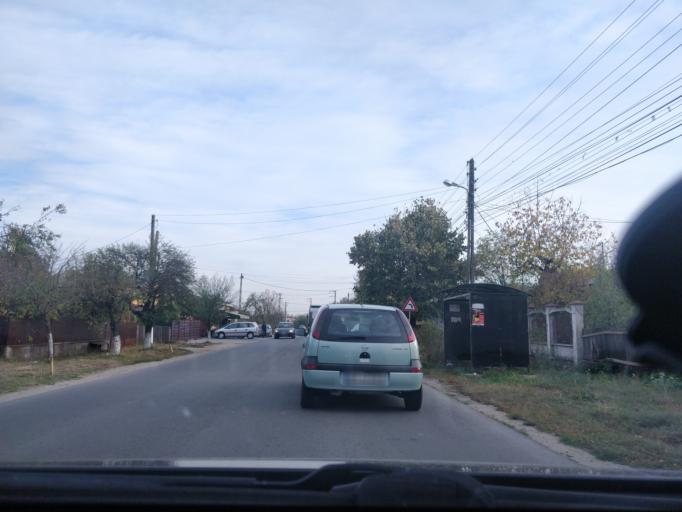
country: RO
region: Giurgiu
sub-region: Comuna Bolintin Vale
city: Malu Spart
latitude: 44.4356
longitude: 25.7220
